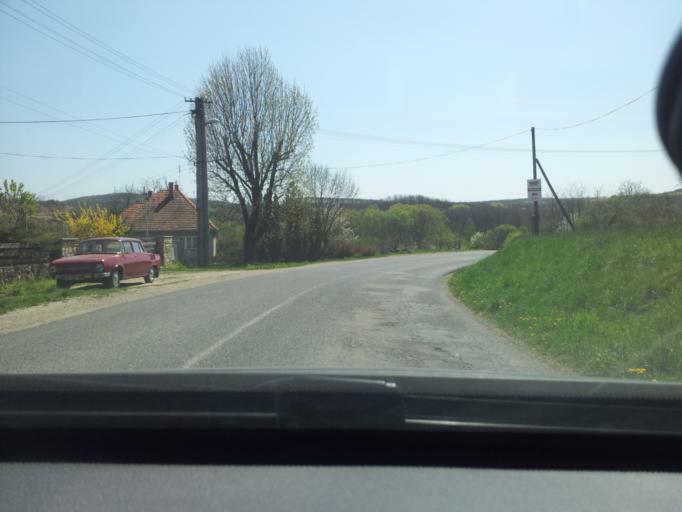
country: SK
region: Nitriansky
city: Tlmace
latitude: 48.3075
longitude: 18.4461
